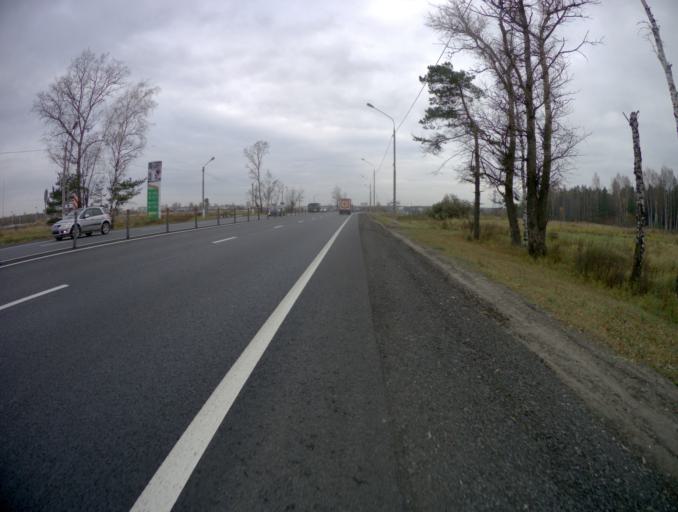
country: RU
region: Moskovskaya
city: Malaya Dubna
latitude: 55.8707
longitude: 38.9635
